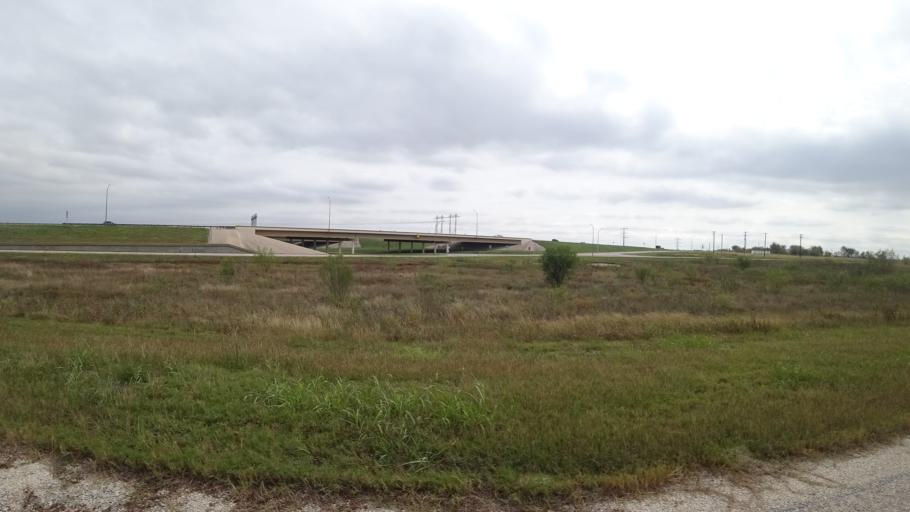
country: US
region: Texas
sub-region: Travis County
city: Pflugerville
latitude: 30.4055
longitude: -97.5851
